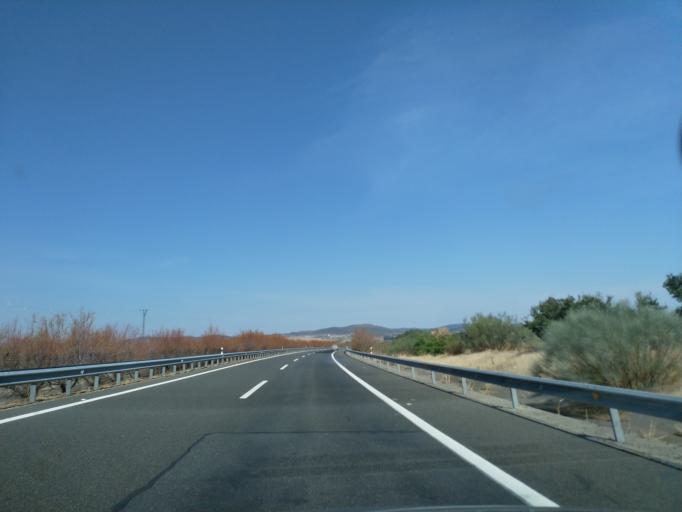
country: ES
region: Extremadura
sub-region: Provincia de Caceres
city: Aldea del Cano
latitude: 39.3470
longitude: -6.3426
